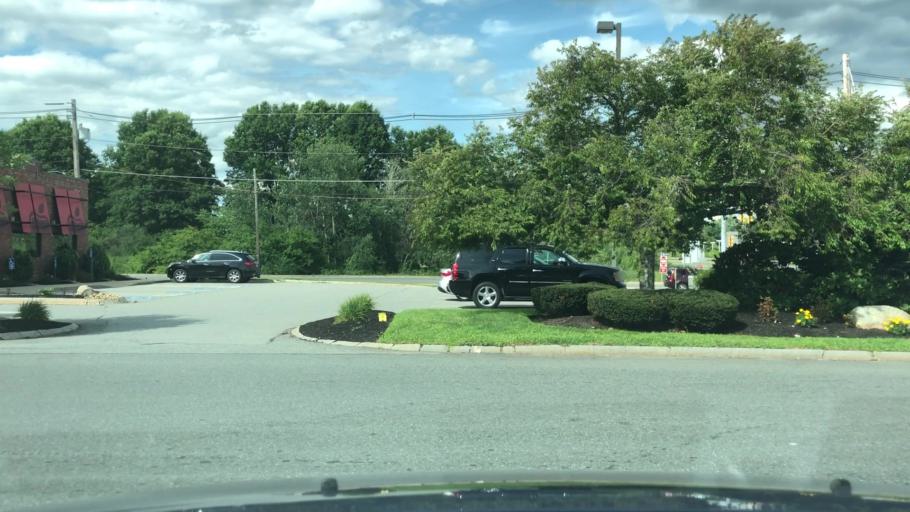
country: US
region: Massachusetts
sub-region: Middlesex County
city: Tewksbury
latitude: 42.6265
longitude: -71.2707
